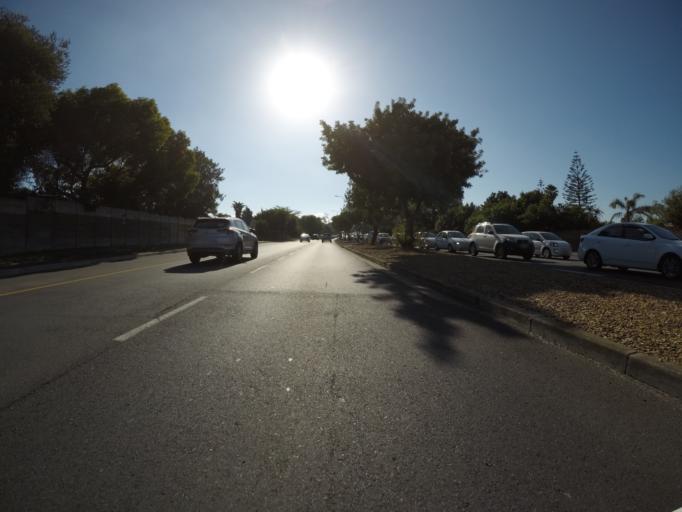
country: ZA
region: Western Cape
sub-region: City of Cape Town
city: Kraaifontein
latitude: -33.8735
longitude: 18.6536
